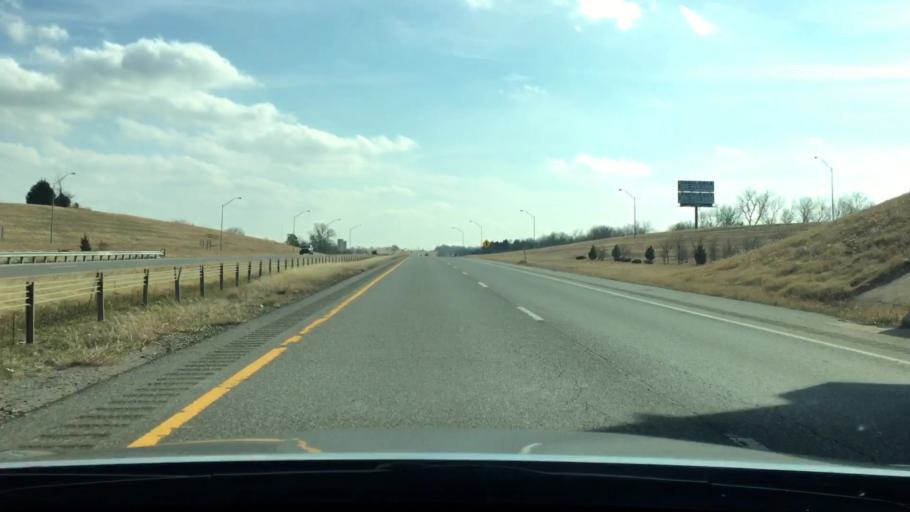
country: US
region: Oklahoma
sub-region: McClain County
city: Purcell
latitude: 34.9822
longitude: -97.3727
